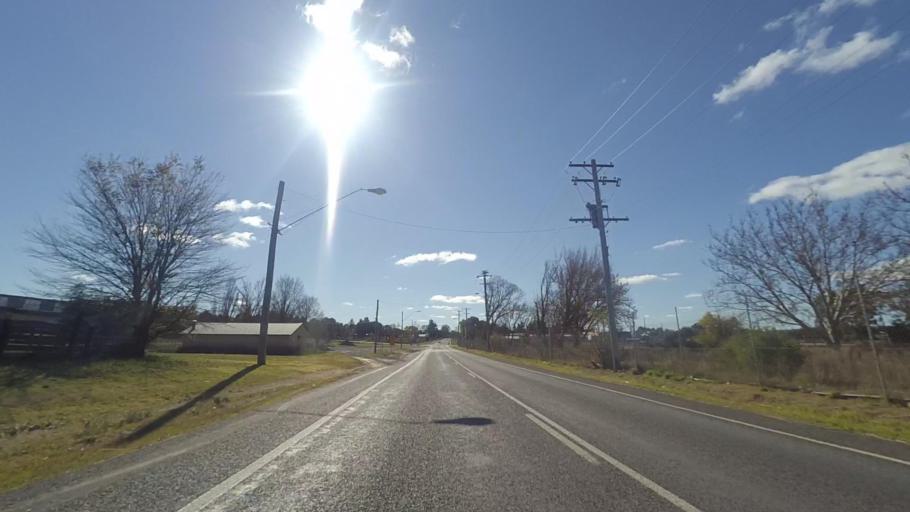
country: AU
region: New South Wales
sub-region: Bathurst Regional
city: Bathurst
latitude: -33.4418
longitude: 149.5787
